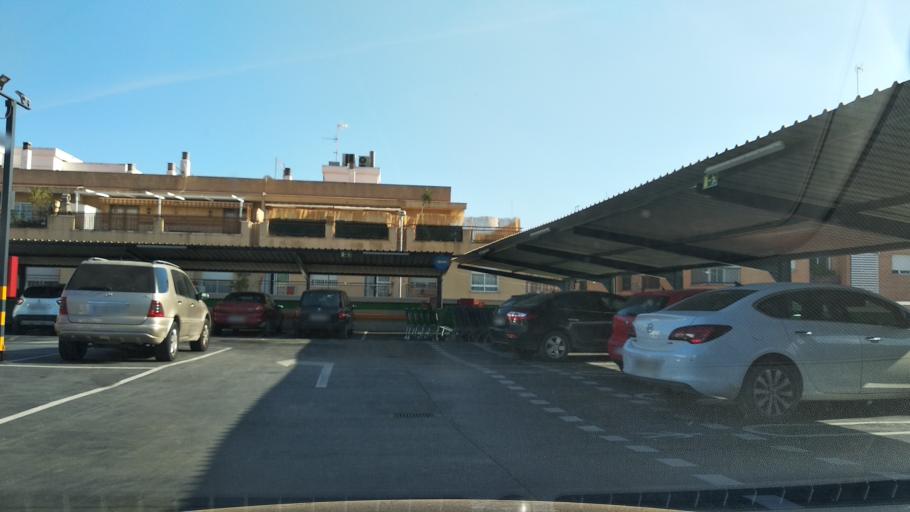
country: ES
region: Murcia
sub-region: Murcia
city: Santomera
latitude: 38.0638
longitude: -1.0522
